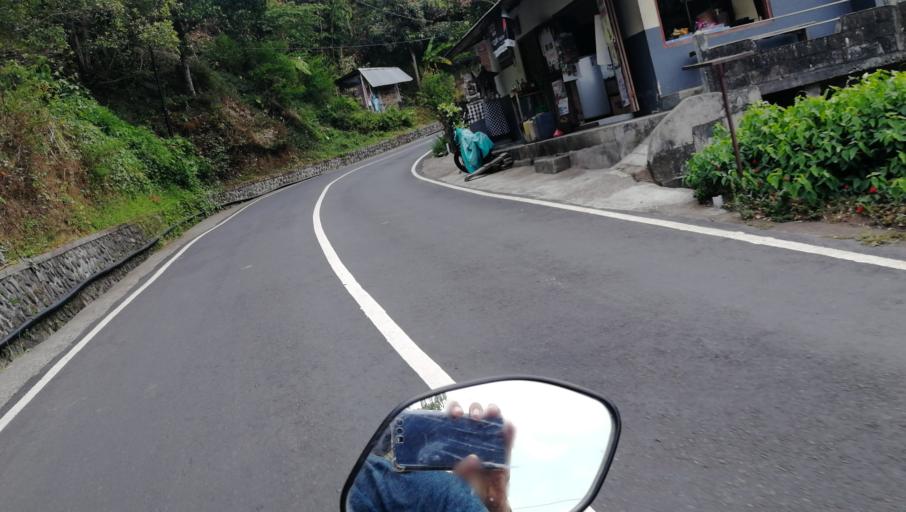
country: ID
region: Bali
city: Munduk
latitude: -8.2645
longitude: 115.0605
